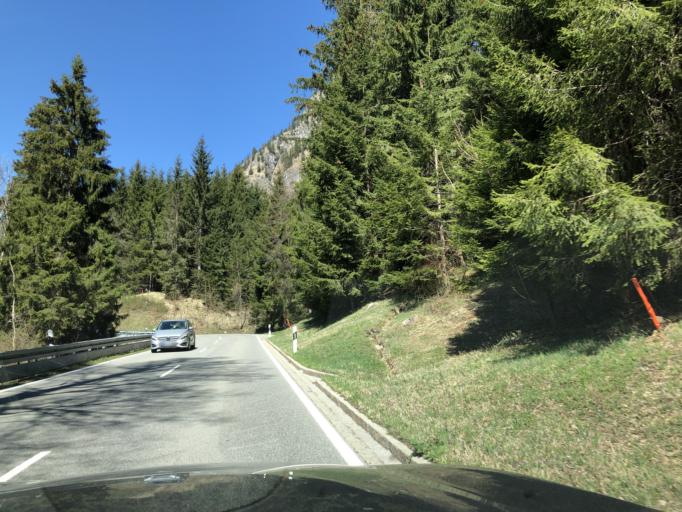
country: AT
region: Tyrol
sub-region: Politischer Bezirk Reutte
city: Schattwald
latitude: 47.5094
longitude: 10.3849
